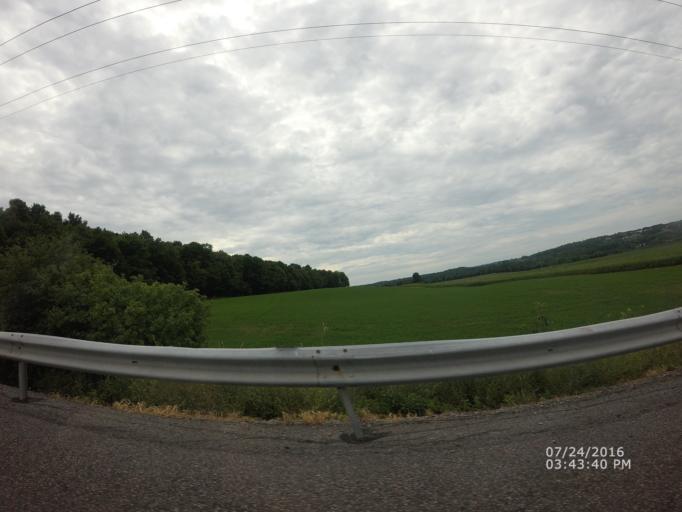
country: US
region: New York
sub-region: Onondaga County
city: Camillus
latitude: 43.0278
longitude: -76.3041
